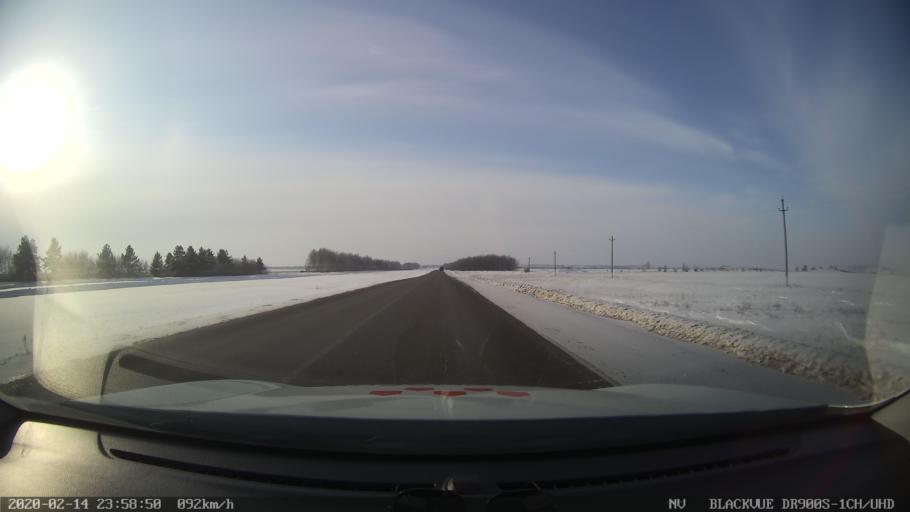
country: RU
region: Tatarstan
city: Kuybyshevskiy Zaton
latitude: 55.3421
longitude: 49.0783
